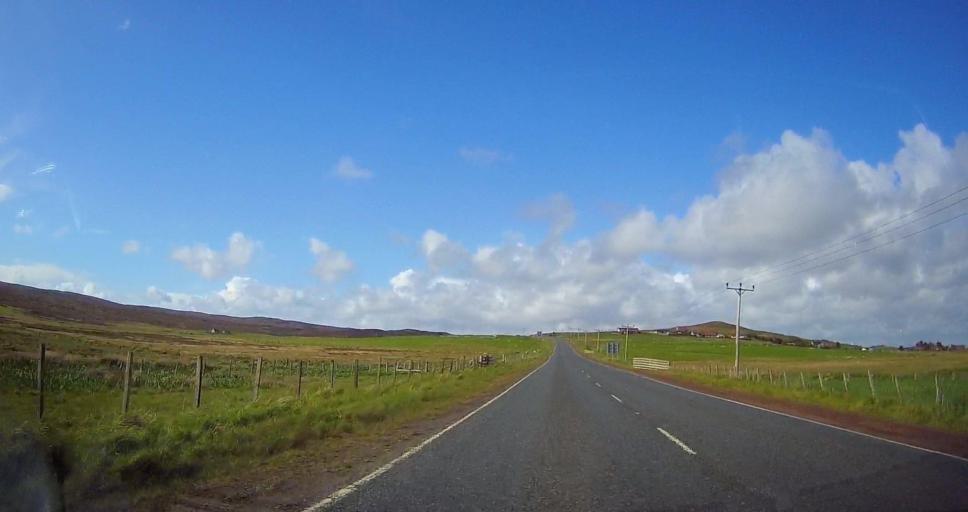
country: GB
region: Scotland
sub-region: Shetland Islands
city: Lerwick
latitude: 60.1928
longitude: -1.2321
